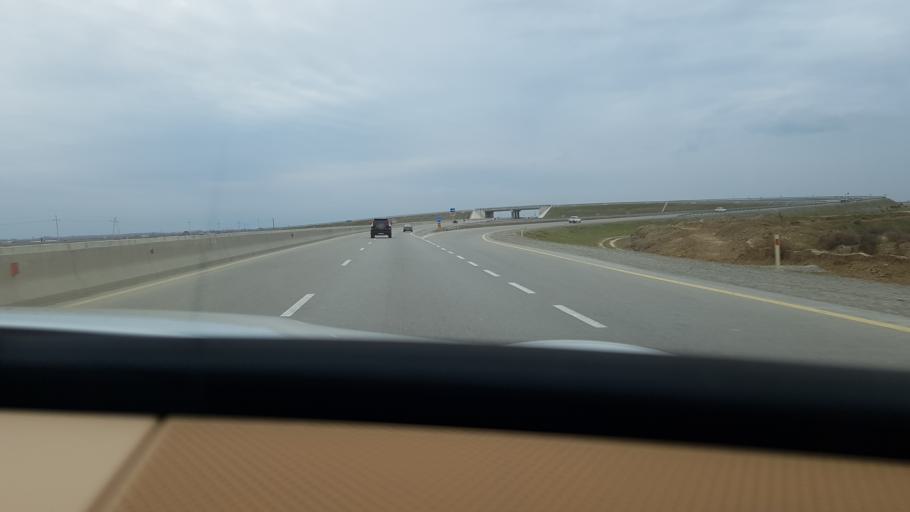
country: AZ
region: Haciqabul
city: Haciqabul
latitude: 40.0085
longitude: 48.9119
